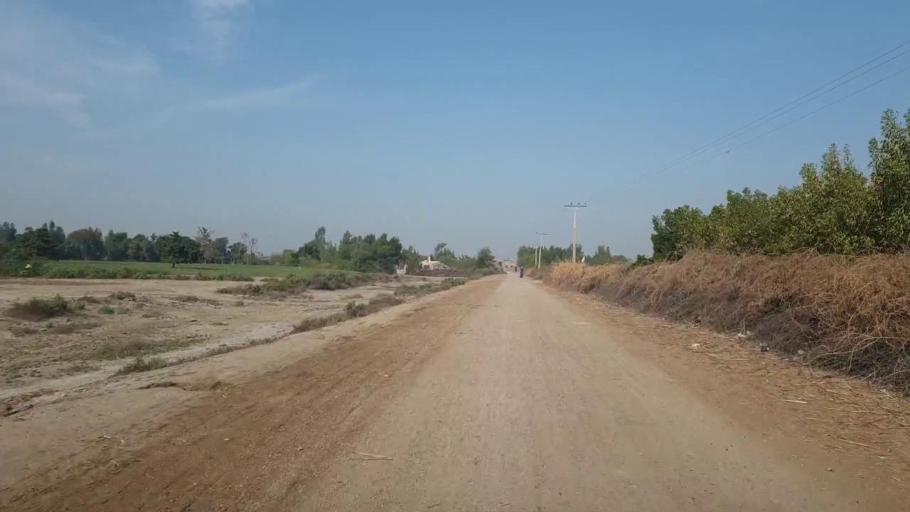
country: PK
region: Sindh
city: Mirwah Gorchani
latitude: 25.3762
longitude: 69.1601
